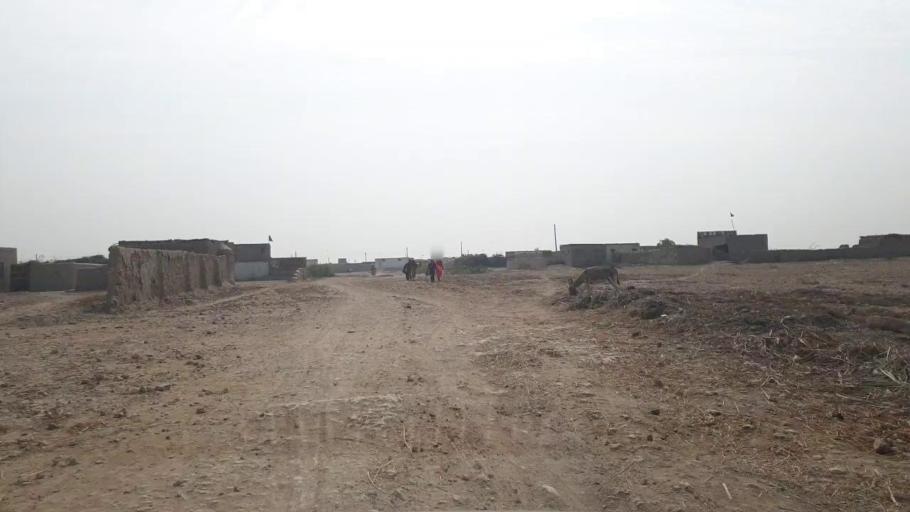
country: PK
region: Sindh
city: Tando Muhammad Khan
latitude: 25.1592
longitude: 68.4705
